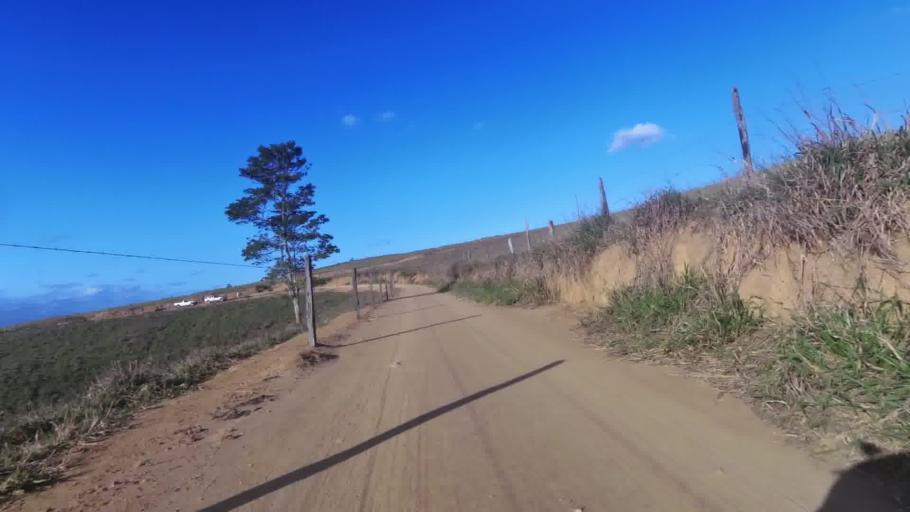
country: BR
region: Espirito Santo
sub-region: Marataizes
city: Marataizes
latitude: -21.1536
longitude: -41.0338
